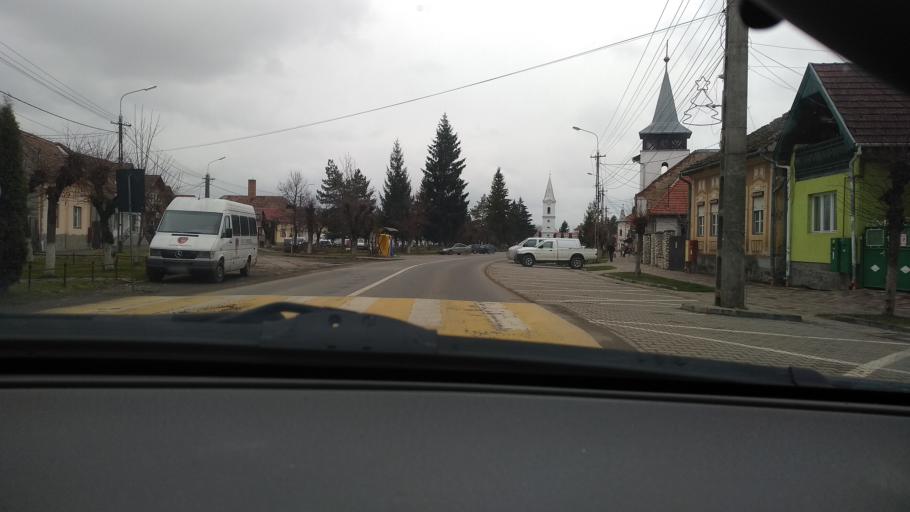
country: RO
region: Mures
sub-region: Comuna Miercurea Nirajului
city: Miercurea Nirajului
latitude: 46.5351
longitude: 24.8024
